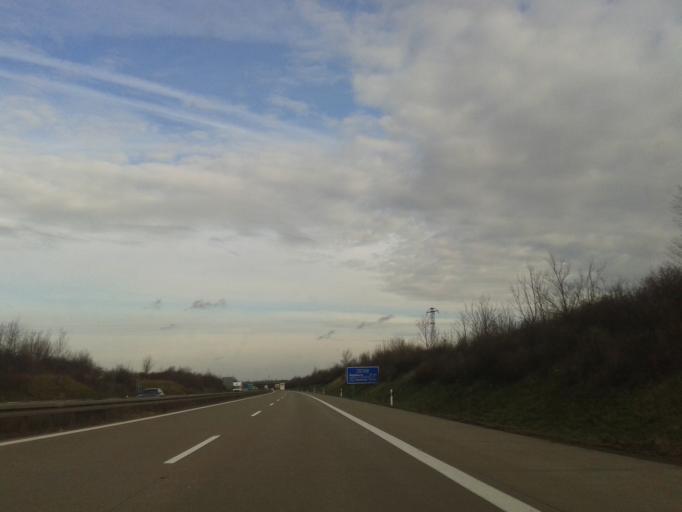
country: DE
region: Saxony-Anhalt
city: Glothe
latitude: 51.9010
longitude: 11.6935
